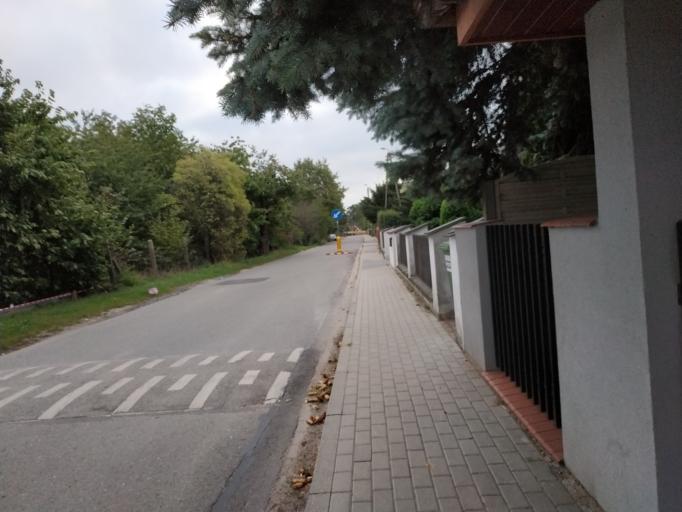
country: PL
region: Lower Silesian Voivodeship
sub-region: Powiat wroclawski
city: Tyniec Maly
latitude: 51.0205
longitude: 16.9144
